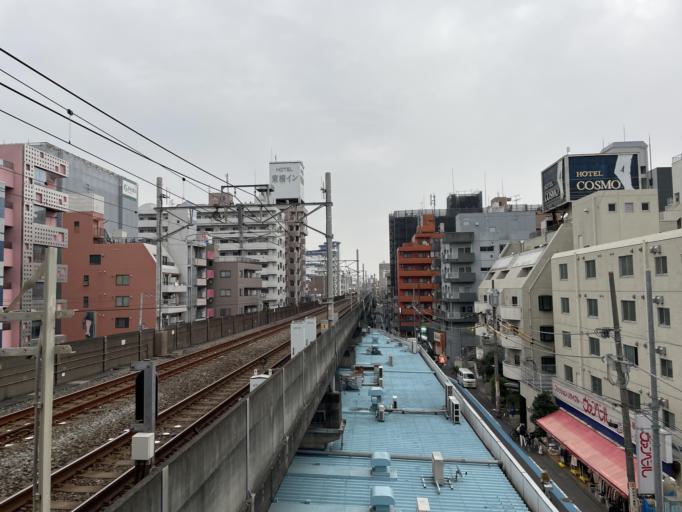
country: JP
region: Tokyo
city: Urayasu
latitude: 35.6645
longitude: 139.8604
